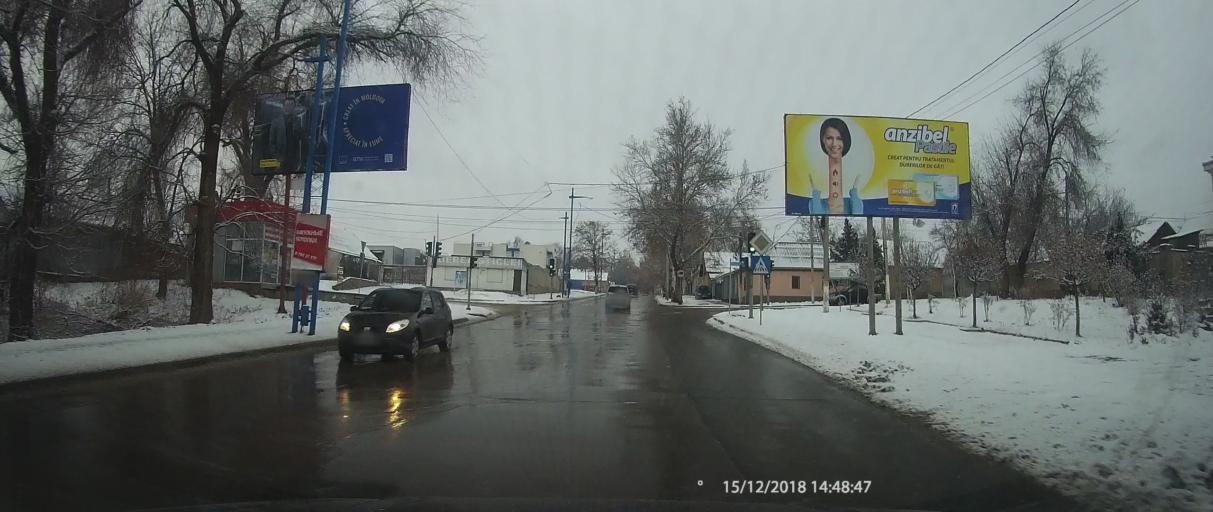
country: MD
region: Cahul
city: Cahul
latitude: 45.9000
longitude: 28.1962
